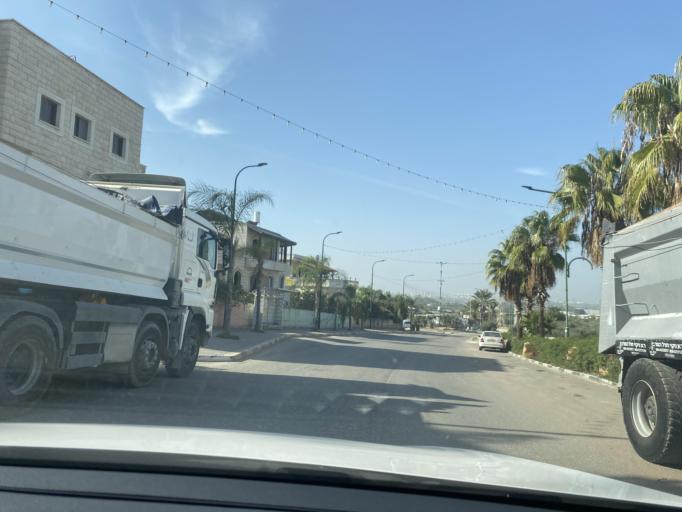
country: IL
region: Central District
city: Kafr Qasim
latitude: 32.1317
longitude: 34.9660
